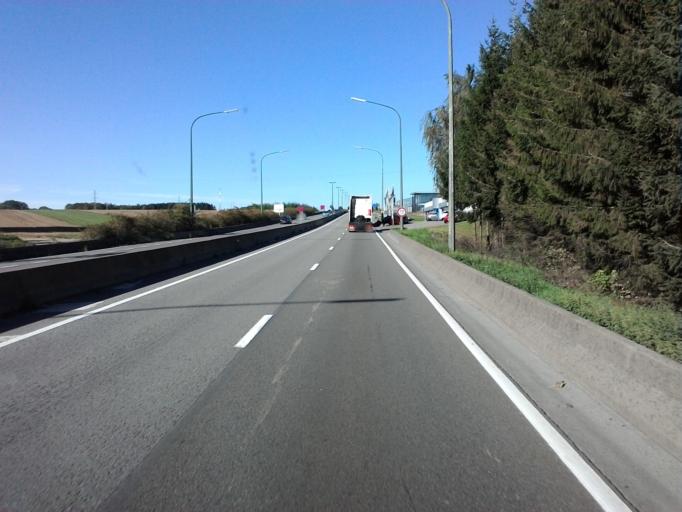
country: BE
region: Wallonia
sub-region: Province du Luxembourg
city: Arlon
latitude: 49.6448
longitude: 5.8172
